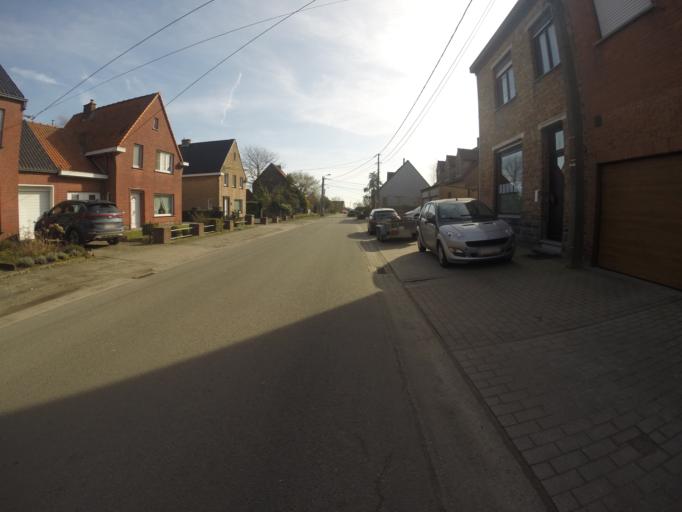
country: BE
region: Flanders
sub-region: Provincie West-Vlaanderen
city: Oostkamp
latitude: 51.1490
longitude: 3.2662
